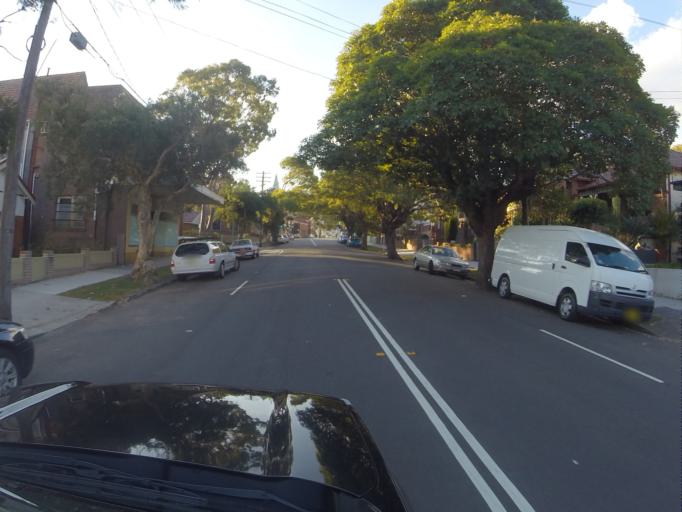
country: AU
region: New South Wales
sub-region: Ashfield
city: Ashfield
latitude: -33.8915
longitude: 151.1254
